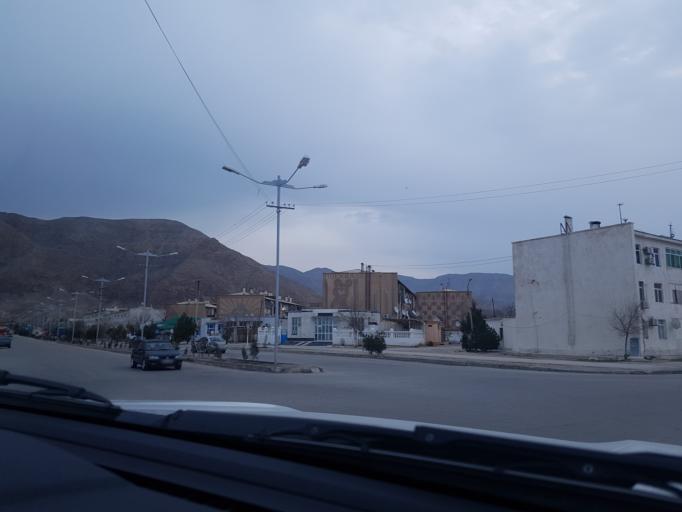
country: TM
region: Balkan
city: Balkanabat
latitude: 39.5199
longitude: 54.3604
